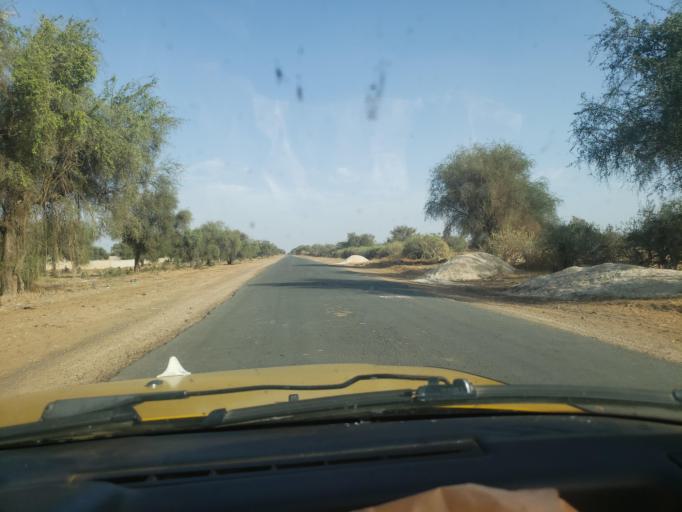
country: SN
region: Louga
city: Louga
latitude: 15.5105
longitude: -15.9832
